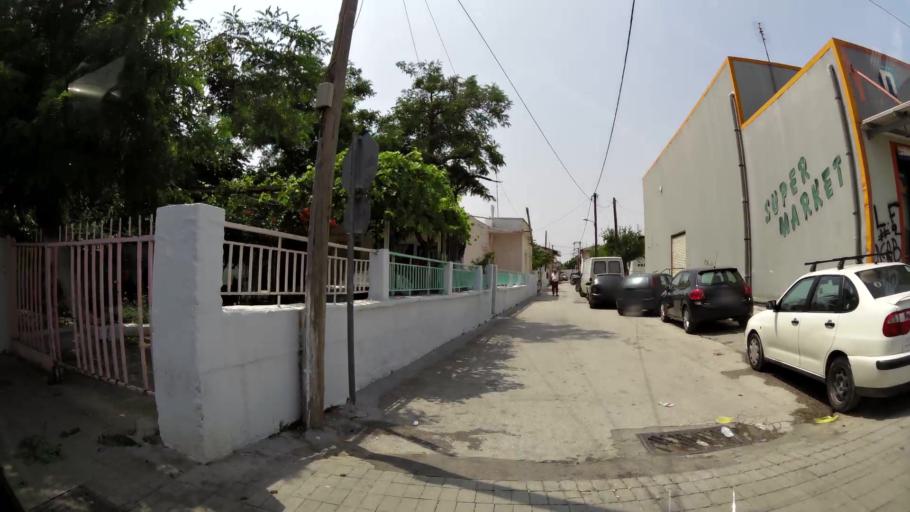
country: GR
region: Central Macedonia
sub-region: Nomos Thessalonikis
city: Menemeni
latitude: 40.6576
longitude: 22.8968
